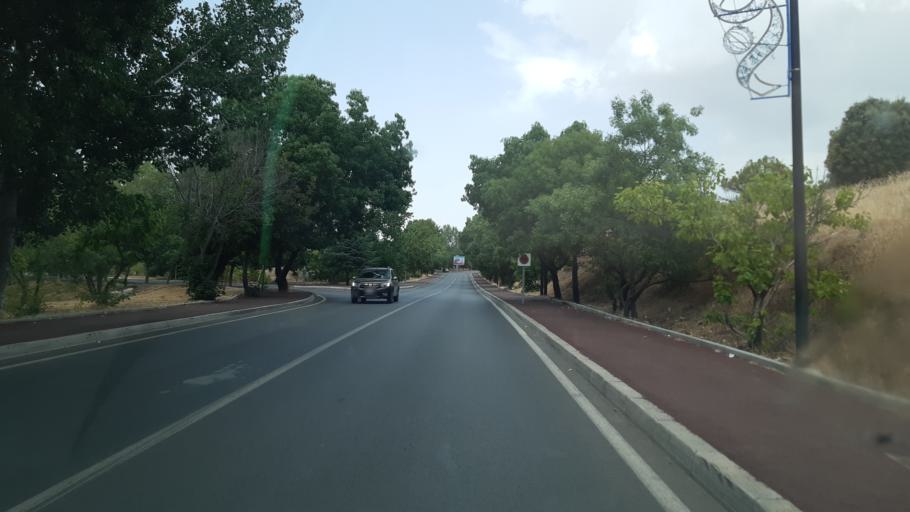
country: MA
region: Meknes-Tafilalet
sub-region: Ifrane
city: Ifrane
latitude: 33.5173
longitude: -5.1173
